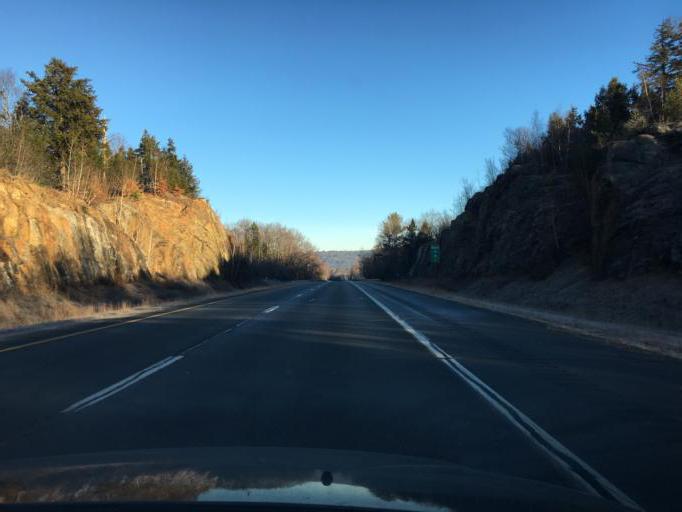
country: US
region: New Hampshire
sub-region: Belknap County
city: Sanbornton
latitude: 43.5533
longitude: -71.6166
